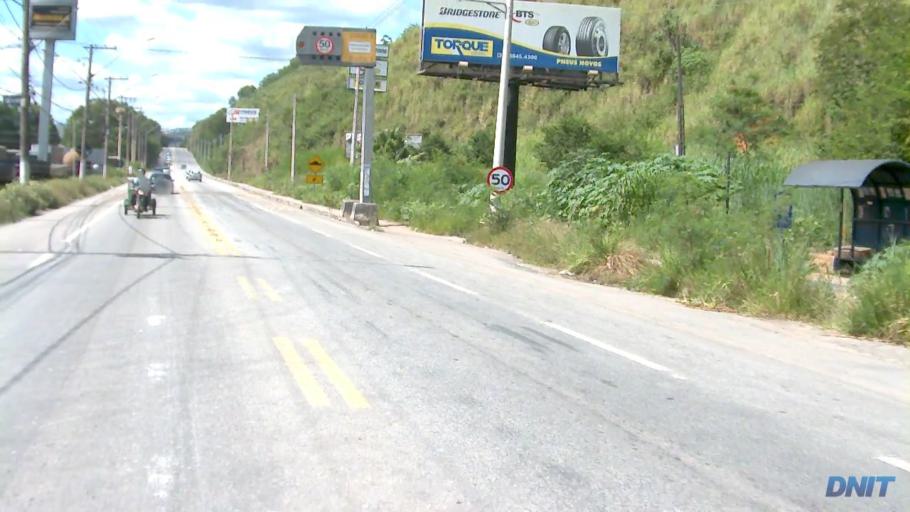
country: BR
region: Minas Gerais
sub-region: Coronel Fabriciano
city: Coronel Fabriciano
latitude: -19.5295
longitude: -42.6609
